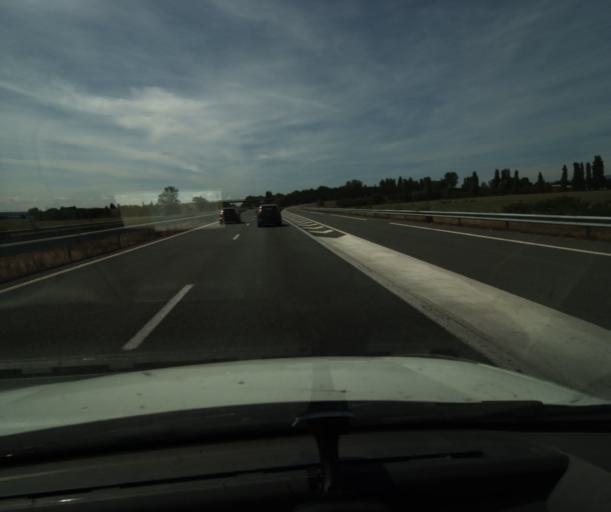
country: FR
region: Languedoc-Roussillon
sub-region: Departement de l'Aude
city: Bram
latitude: 43.2355
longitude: 2.1004
